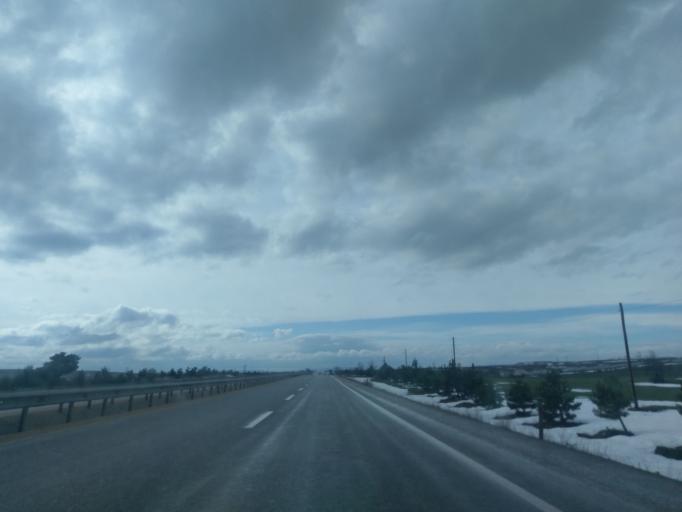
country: TR
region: Eskisehir
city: Inonu
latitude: 39.7230
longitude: 30.2570
